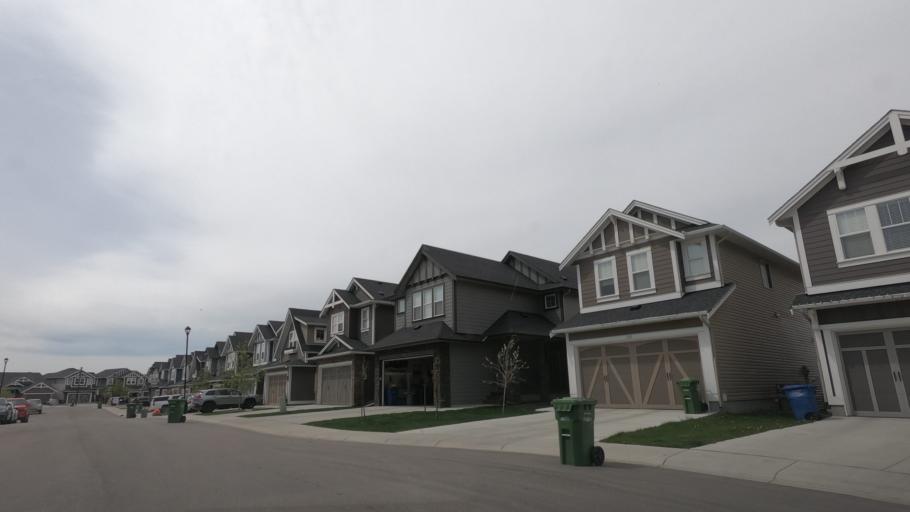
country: CA
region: Alberta
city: Airdrie
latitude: 51.3070
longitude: -114.0319
